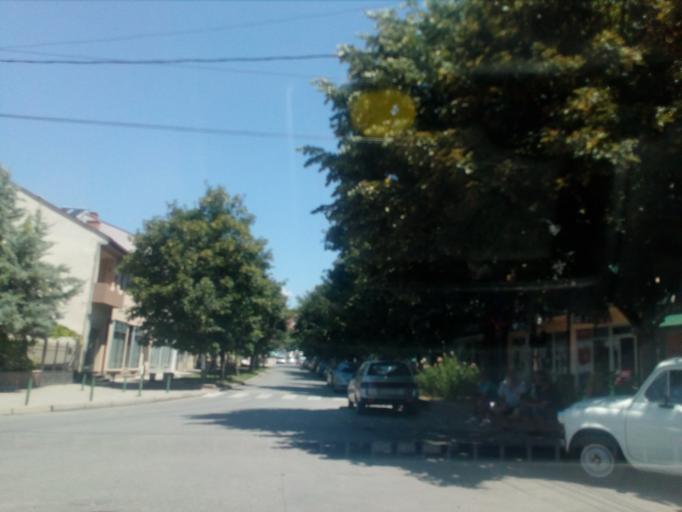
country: MK
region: Veles
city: Veles
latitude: 41.7137
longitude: 21.7869
